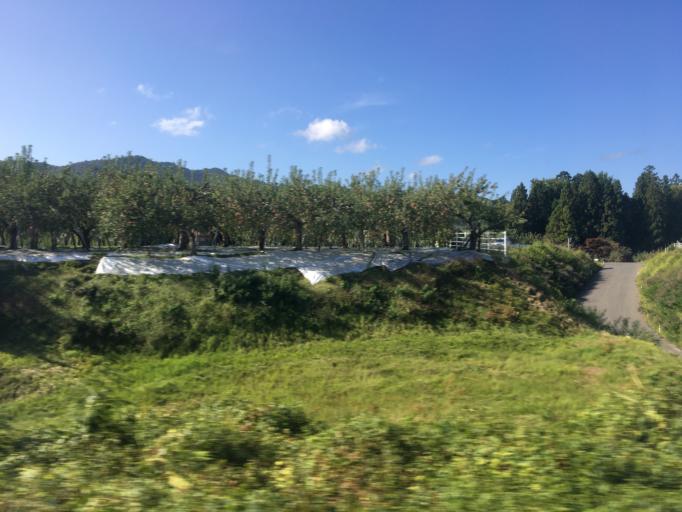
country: JP
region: Aomori
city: Hirosaki
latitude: 40.5501
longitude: 140.5399
